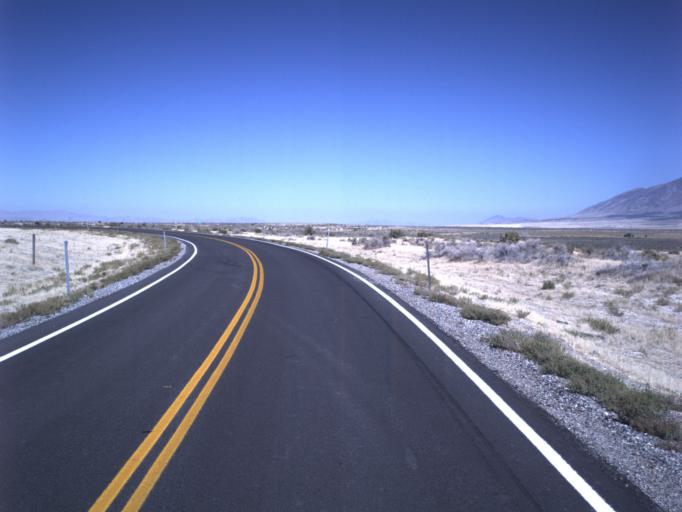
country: US
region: Utah
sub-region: Tooele County
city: Grantsville
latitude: 40.2450
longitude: -112.7232
